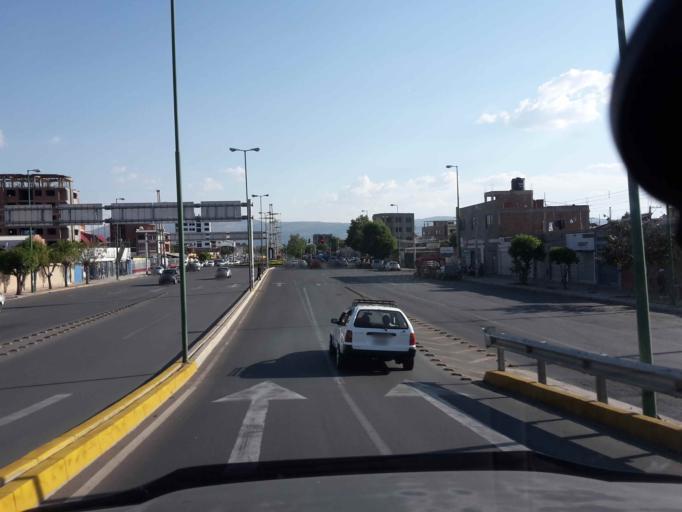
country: BO
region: Cochabamba
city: Cochabamba
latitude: -17.3948
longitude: -66.1847
